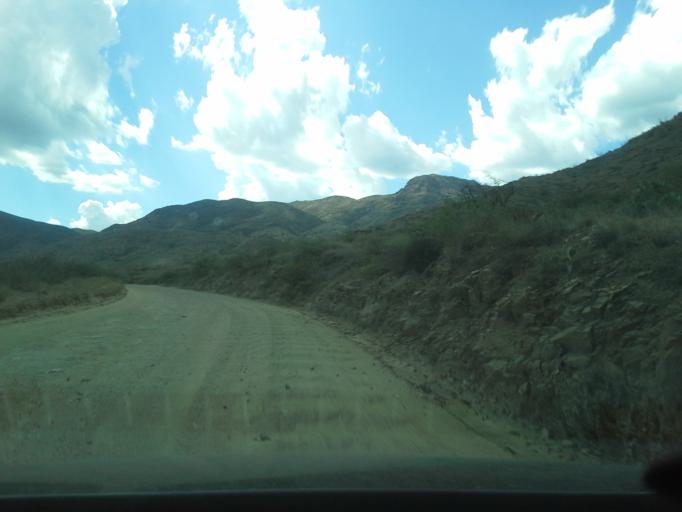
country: US
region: Arizona
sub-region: Yavapai County
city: Mayer
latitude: 34.2755
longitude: -112.2671
